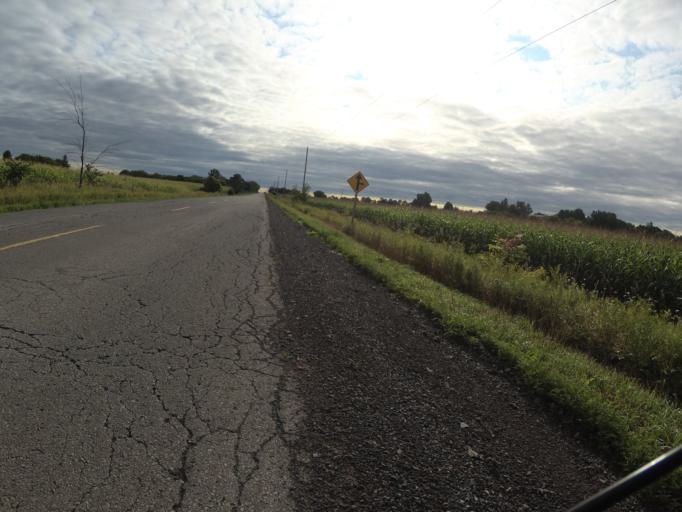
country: CA
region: Ontario
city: Clarence-Rockland
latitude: 45.3215
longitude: -75.3930
